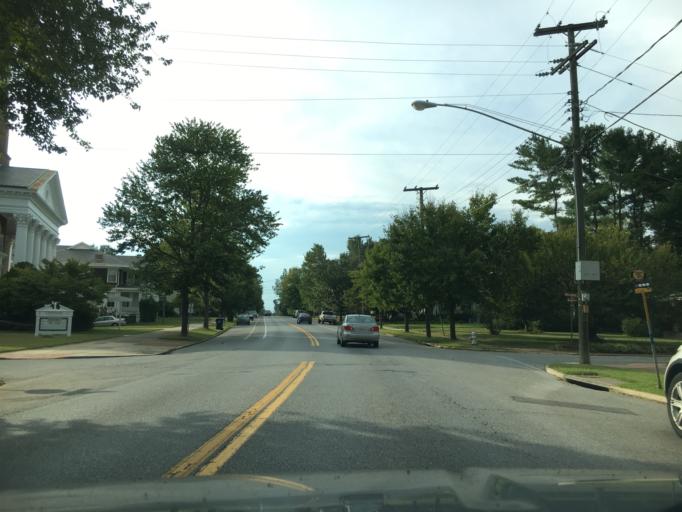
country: US
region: Virginia
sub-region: City of Lynchburg
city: Lynchburg
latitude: 37.4314
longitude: -79.1551
